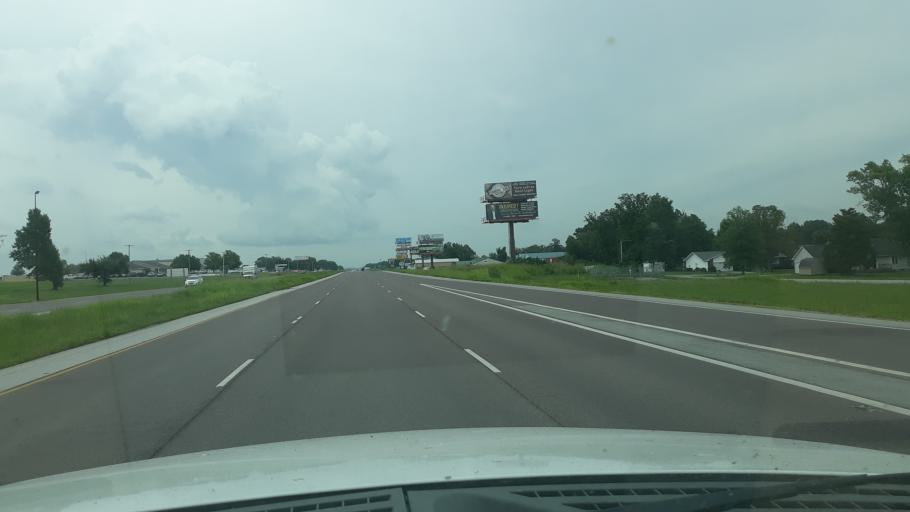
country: US
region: Illinois
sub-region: Williamson County
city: Crainville
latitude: 37.7449
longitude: -89.0539
